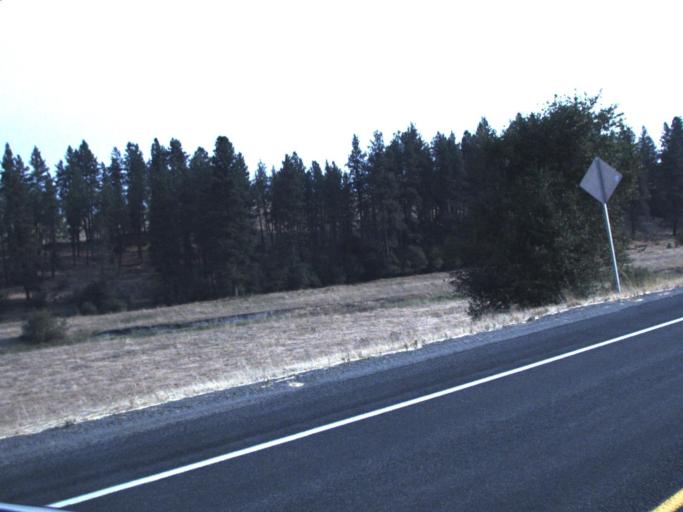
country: US
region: Idaho
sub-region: Benewah County
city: Plummer
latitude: 47.4436
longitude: -117.0756
